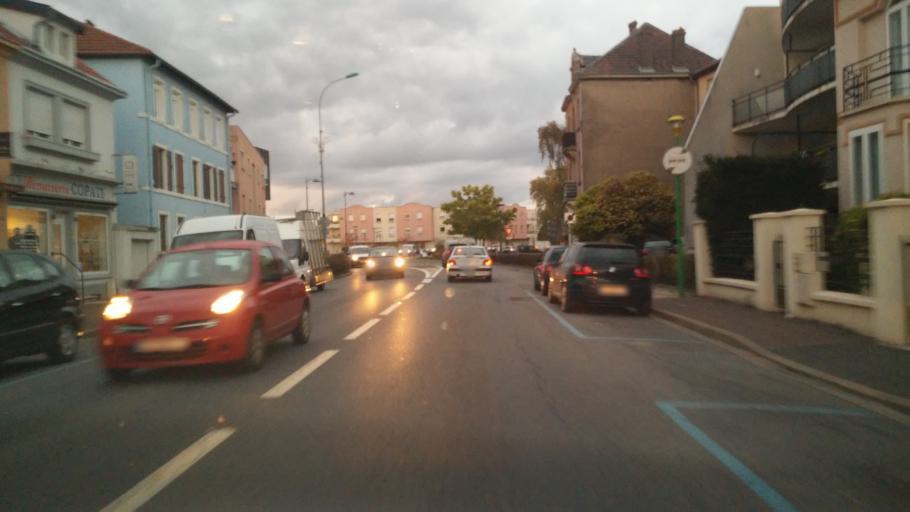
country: FR
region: Lorraine
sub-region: Departement de la Moselle
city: Maizieres-les-Metz
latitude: 49.2144
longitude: 6.1595
